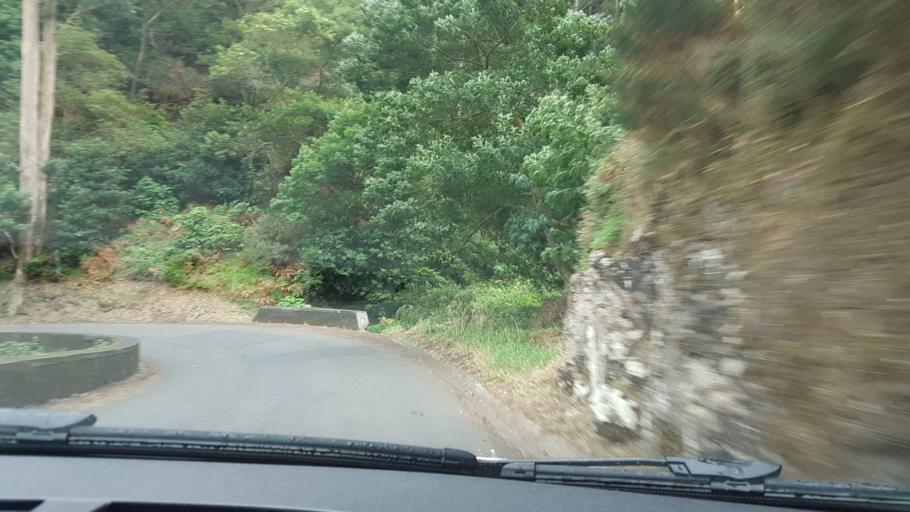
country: PT
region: Madeira
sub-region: Santa Cruz
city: Santa Cruz
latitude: 32.7277
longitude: -16.8097
